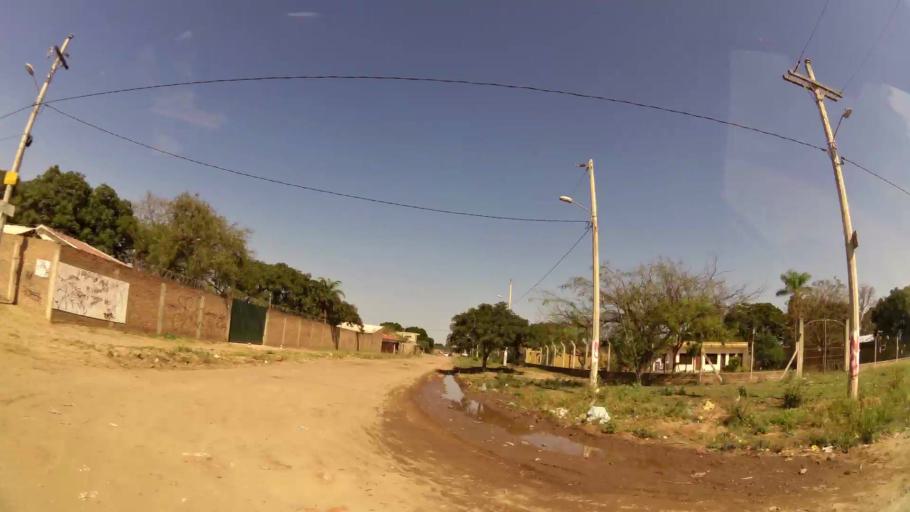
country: BO
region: Santa Cruz
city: Cotoca
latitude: -17.7249
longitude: -63.0836
